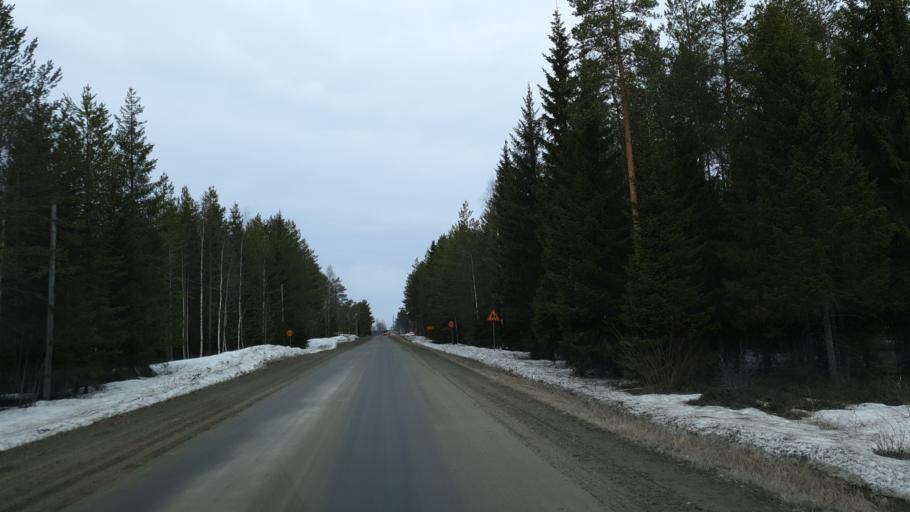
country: SE
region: Vaesterbotten
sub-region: Skelleftea Kommun
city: Burea
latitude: 64.3135
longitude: 21.1407
